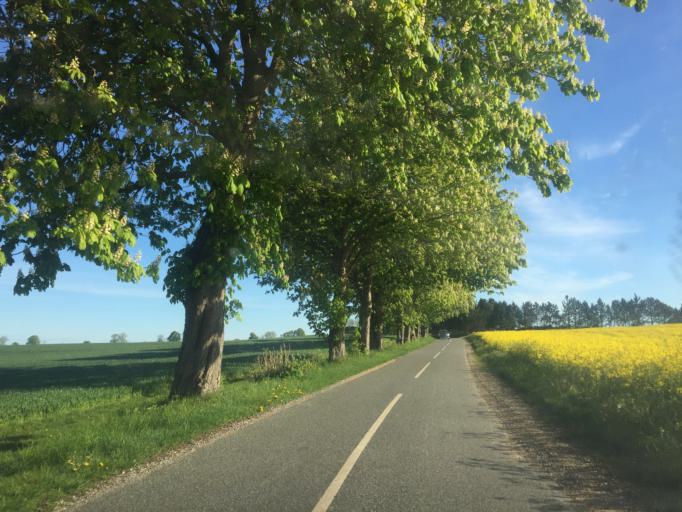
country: DK
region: Capital Region
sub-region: Egedal Kommune
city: Vekso
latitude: 55.7144
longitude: 12.2597
